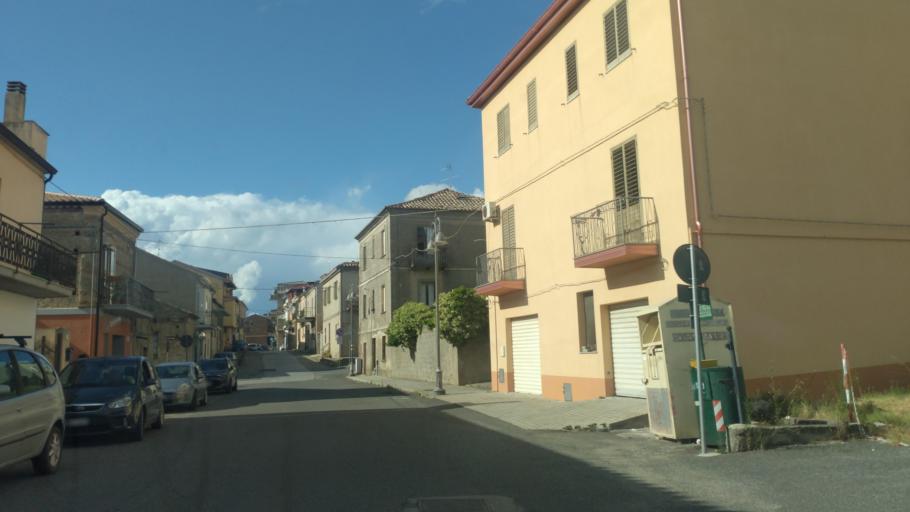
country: IT
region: Calabria
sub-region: Provincia di Catanzaro
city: Staletti
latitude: 38.7635
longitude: 16.5405
